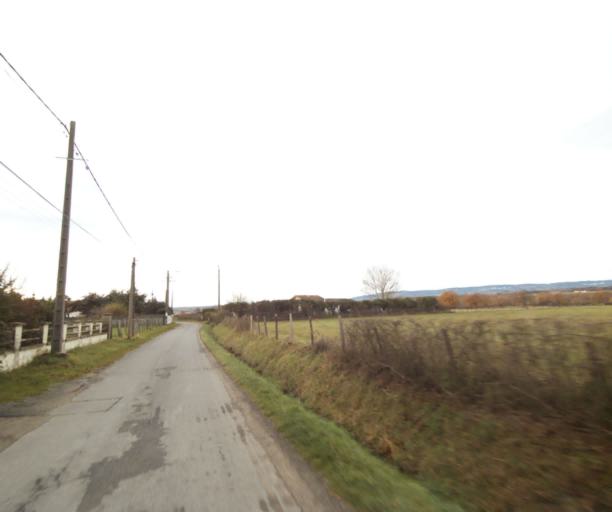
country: FR
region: Rhone-Alpes
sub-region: Departement de la Loire
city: Sury-le-Comtal
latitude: 45.5346
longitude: 4.1672
